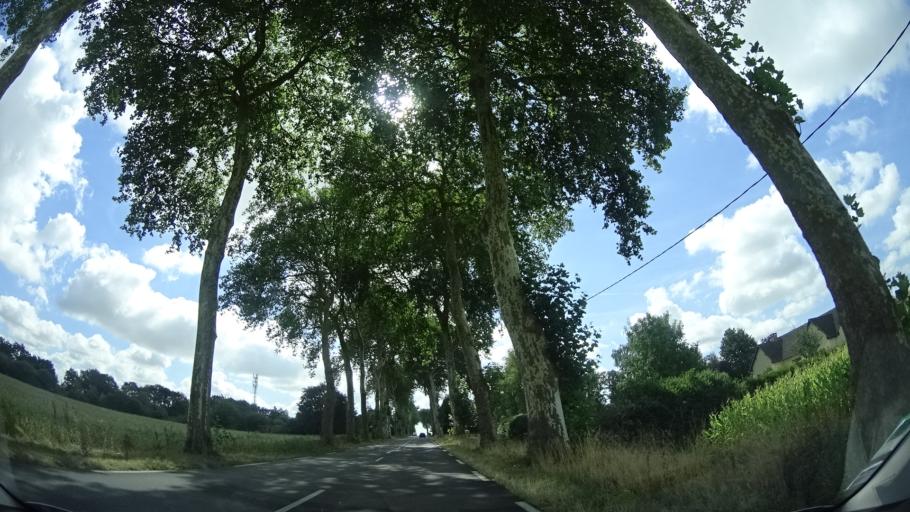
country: FR
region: Pays de la Loire
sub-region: Departement de la Mayenne
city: Meslay-du-Maine
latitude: 47.9575
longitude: -0.5669
